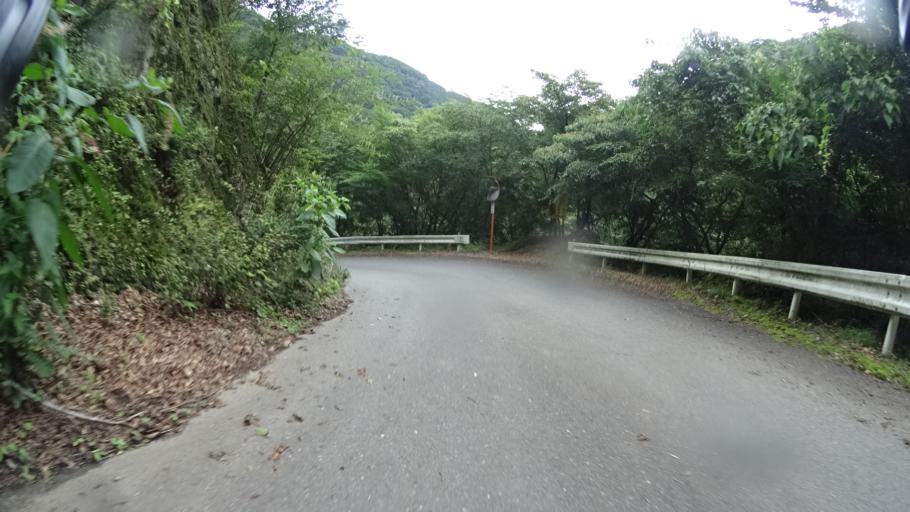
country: JP
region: Saitama
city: Chichibu
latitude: 35.8860
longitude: 139.1374
